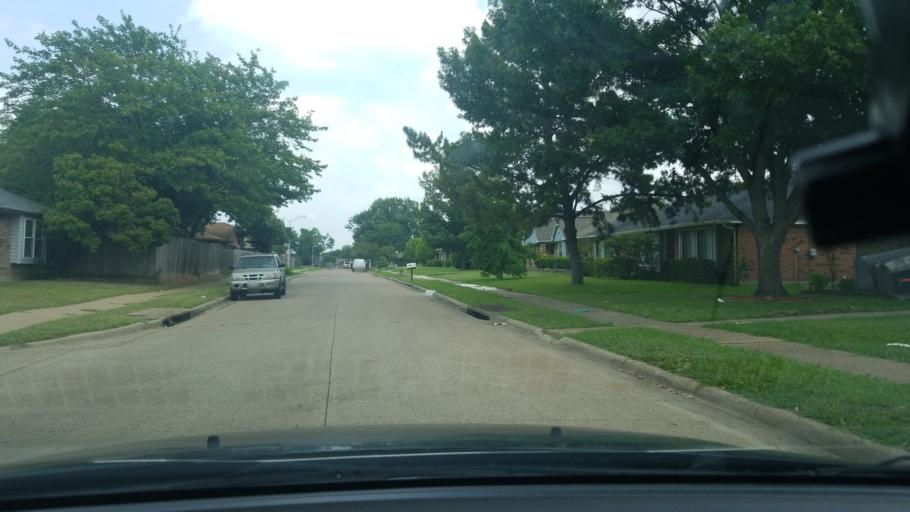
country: US
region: Texas
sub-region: Dallas County
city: Mesquite
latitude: 32.7995
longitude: -96.6187
